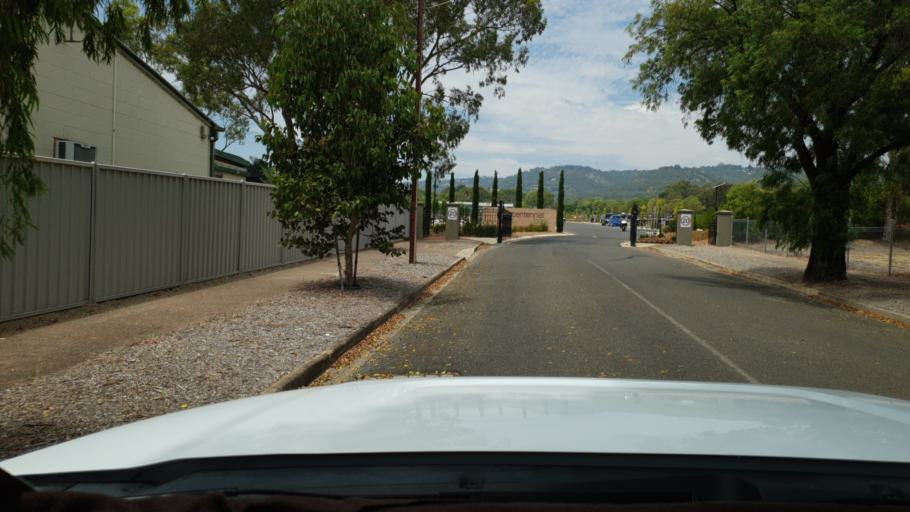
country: AU
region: South Australia
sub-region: Marion
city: Clovelly Park
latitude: -34.9978
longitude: 138.5837
